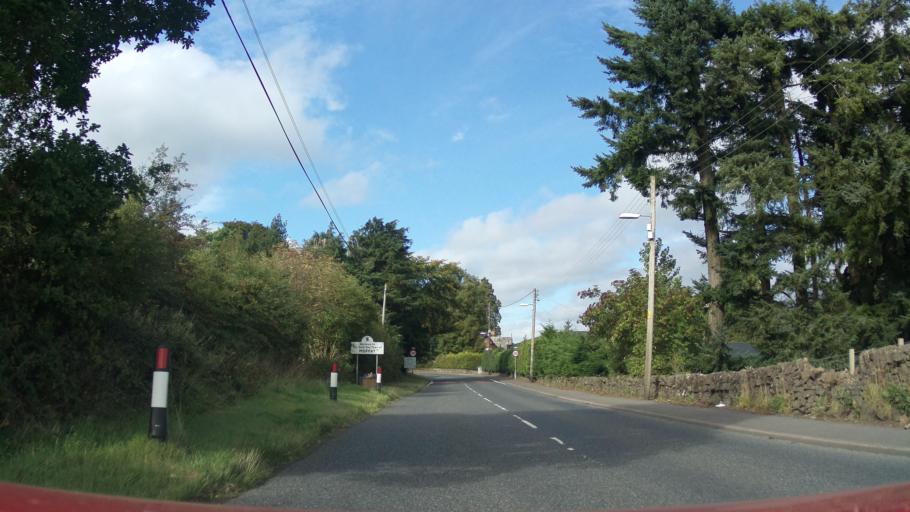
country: GB
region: Scotland
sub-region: Dumfries and Galloway
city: Moffat
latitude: 55.3240
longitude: -3.4467
